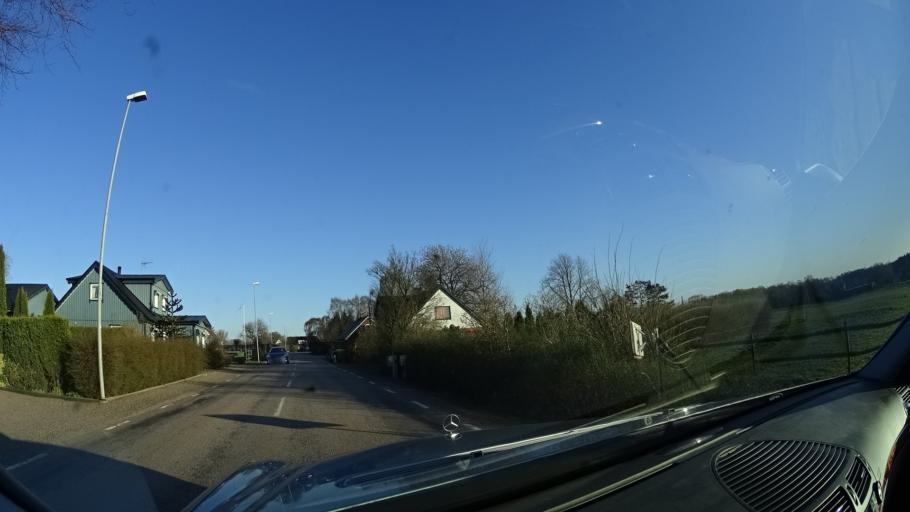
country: SE
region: Skane
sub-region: Bjuvs Kommun
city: Billesholm
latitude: 56.0493
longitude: 13.0003
